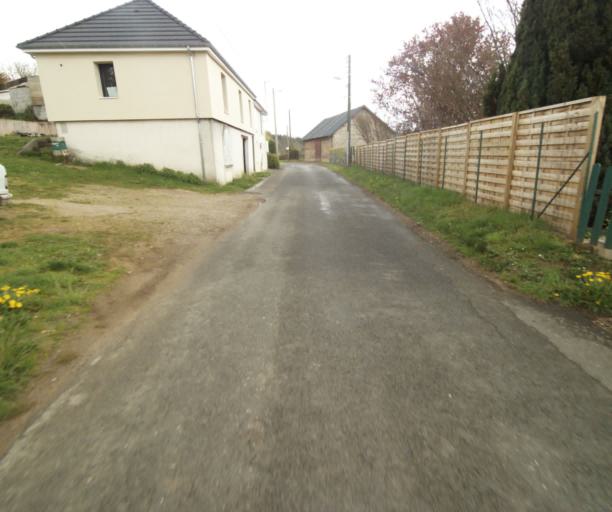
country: FR
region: Limousin
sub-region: Departement de la Correze
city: Tulle
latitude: 45.2771
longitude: 1.7473
